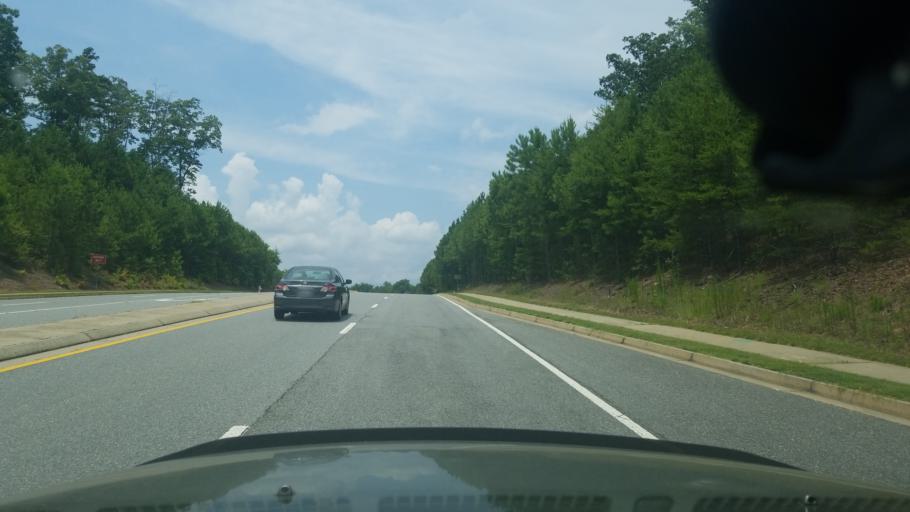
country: US
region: Georgia
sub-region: Fulton County
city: Johns Creek
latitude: 34.0957
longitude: -84.1646
